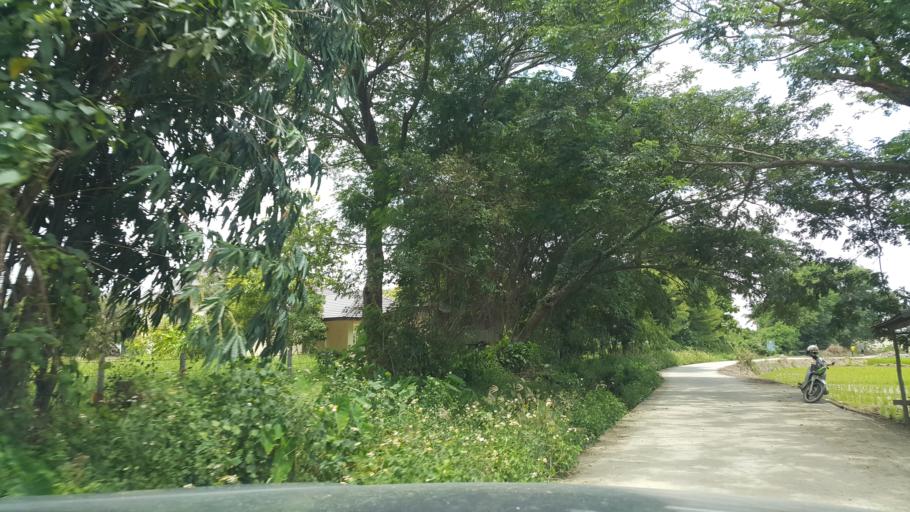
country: TH
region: Chiang Mai
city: Saraphi
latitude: 18.7321
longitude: 98.9932
